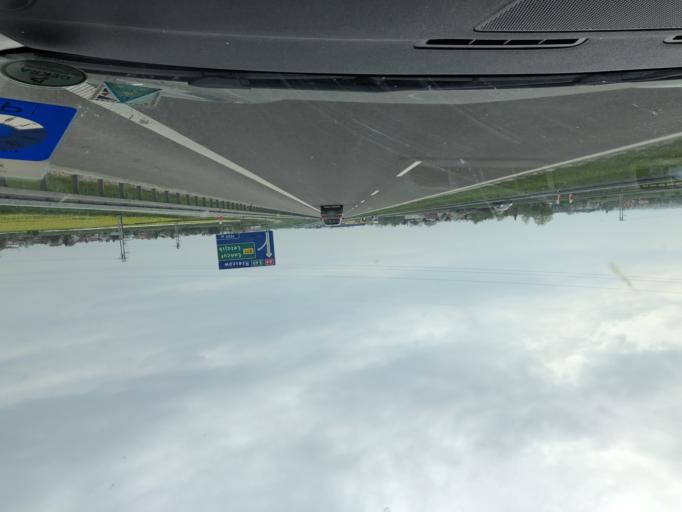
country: PL
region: Subcarpathian Voivodeship
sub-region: Powiat lancucki
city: Gluchow
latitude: 50.0996
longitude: 22.2493
